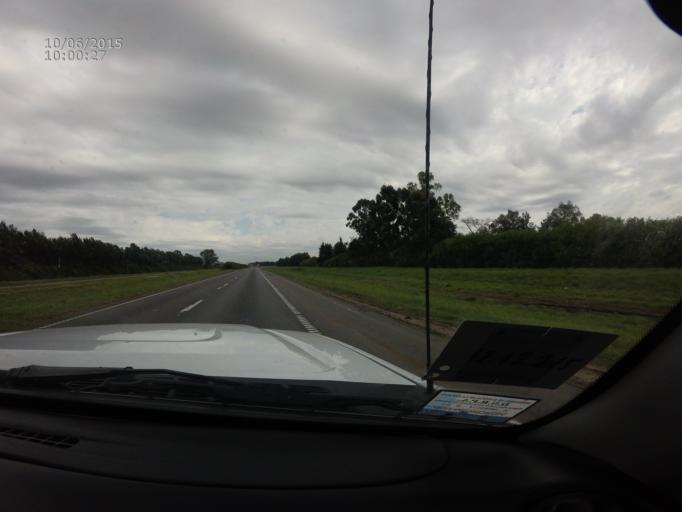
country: AR
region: Buenos Aires
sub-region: Partido de Baradero
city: Baradero
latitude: -33.8944
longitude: -59.4793
